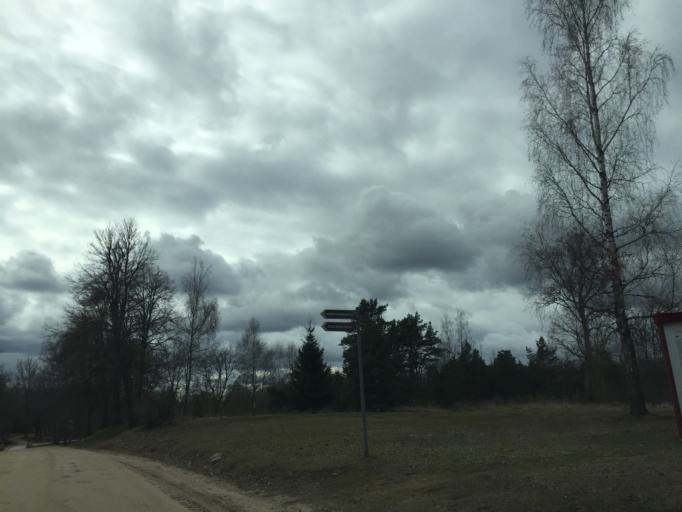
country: LV
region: Akniste
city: Akniste
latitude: 56.1005
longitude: 25.8176
